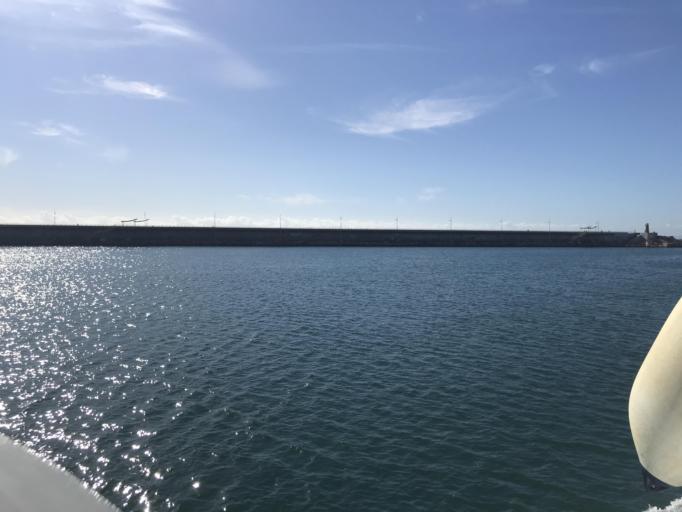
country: ES
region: Valencia
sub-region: Provincia de Alicante
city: Torrevieja
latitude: 37.9680
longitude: -0.6867
